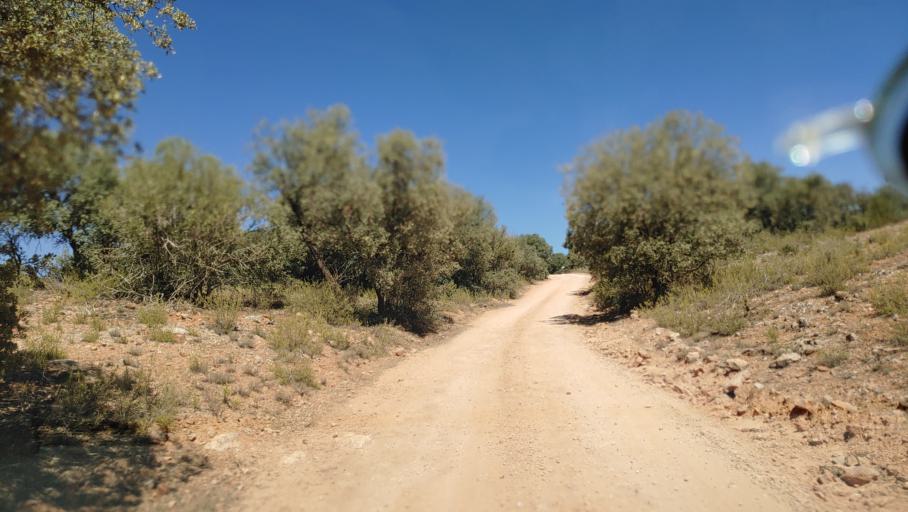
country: ES
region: Castille-La Mancha
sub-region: Provincia de Albacete
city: Ossa de Montiel
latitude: 38.9185
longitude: -2.8000
